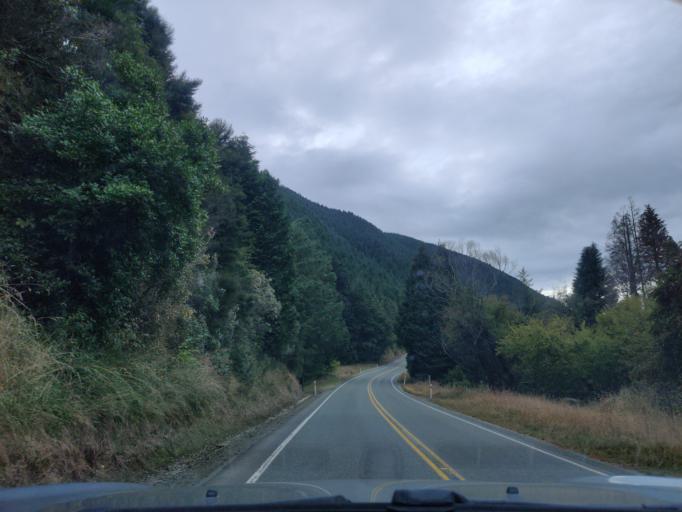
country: NZ
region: Tasman
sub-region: Tasman District
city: Wakefield
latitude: -41.6976
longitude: 172.6368
